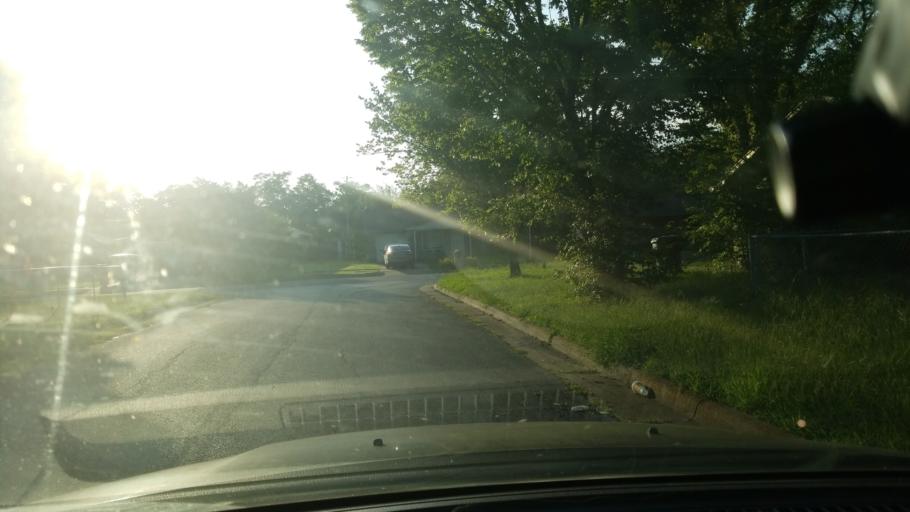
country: US
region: Texas
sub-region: Dallas County
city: Balch Springs
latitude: 32.7232
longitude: -96.6601
